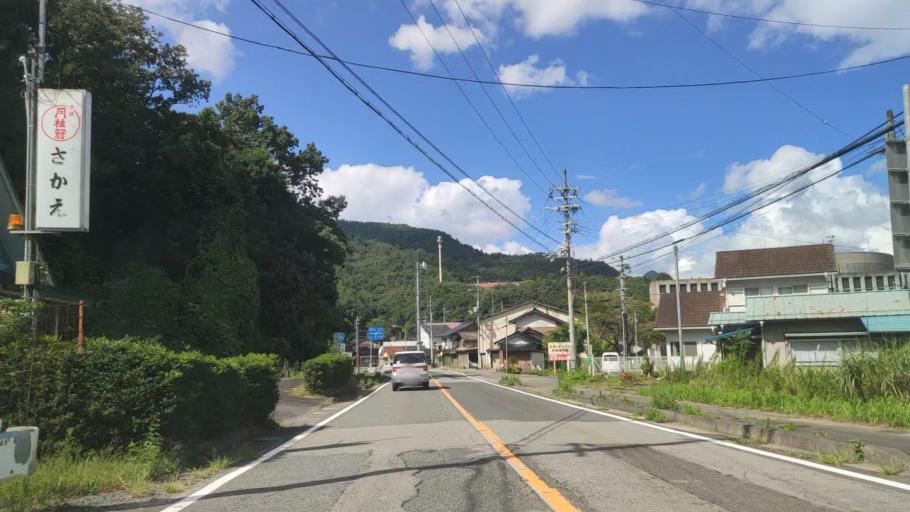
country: JP
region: Hyogo
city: Toyooka
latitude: 35.4690
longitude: 134.9500
